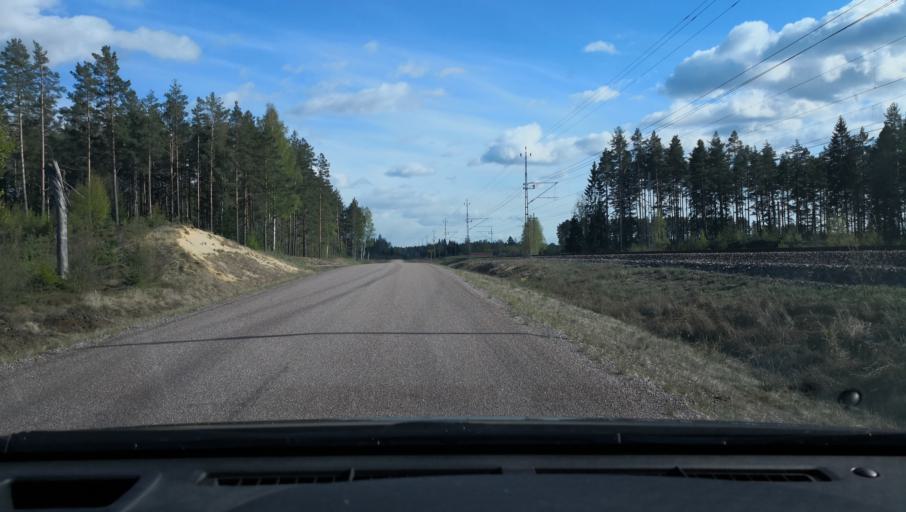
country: SE
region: OErebro
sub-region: Askersunds Kommun
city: Asbro
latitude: 58.9371
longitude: 15.0424
